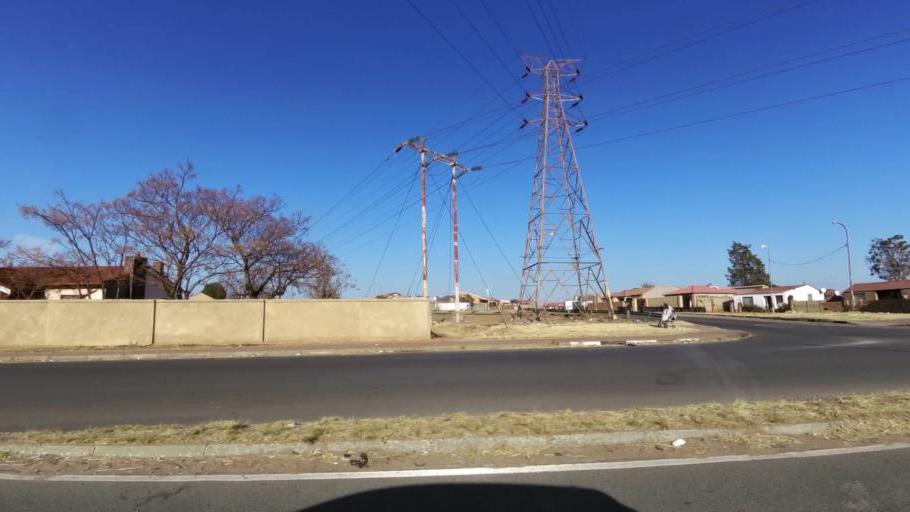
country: ZA
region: Gauteng
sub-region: City of Johannesburg Metropolitan Municipality
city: Soweto
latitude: -26.2336
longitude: 27.9387
